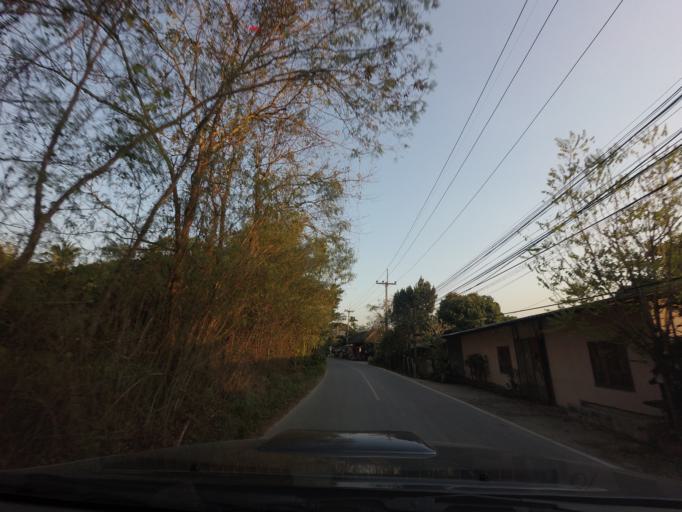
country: TH
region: Chiang Mai
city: Chiang Mai
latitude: 18.9190
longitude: 98.9125
